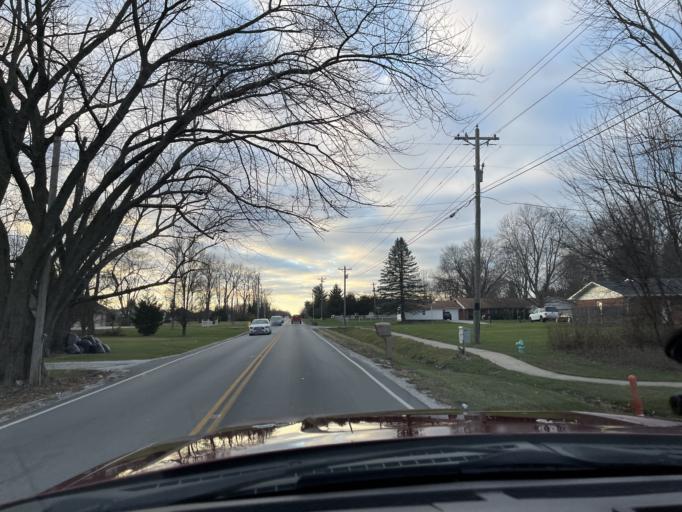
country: US
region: Indiana
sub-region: Hendricks County
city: Avon
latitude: 39.7773
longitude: -86.4034
